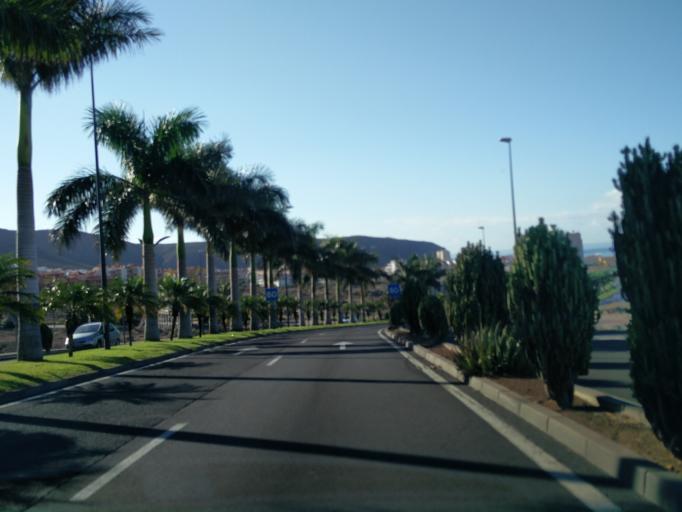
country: ES
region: Canary Islands
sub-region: Provincia de Santa Cruz de Tenerife
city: Playa de las Americas
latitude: 28.0603
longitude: -16.7111
